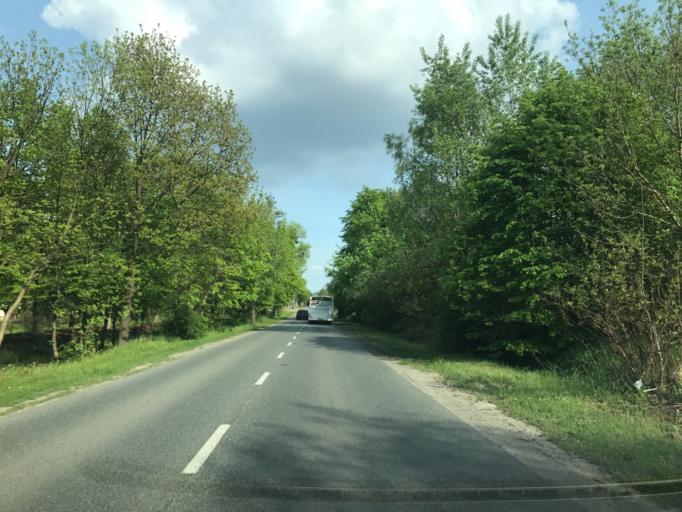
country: PL
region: Kujawsko-Pomorskie
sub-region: Powiat bydgoski
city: Osielsko
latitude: 53.1176
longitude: 18.0910
